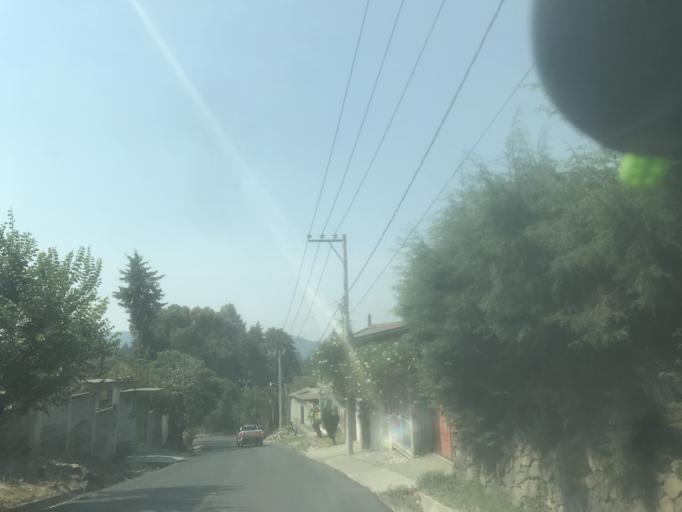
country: MX
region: Mexico
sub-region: Atlautla
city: San Juan Tepecoculco
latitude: 18.9945
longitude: -98.7944
